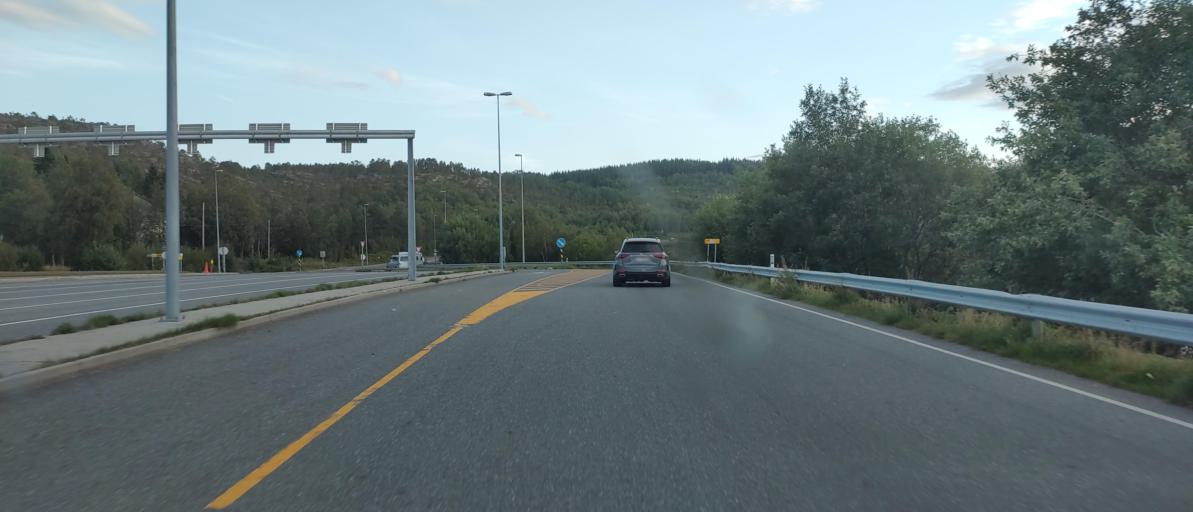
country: NO
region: Nordland
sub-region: Lodingen
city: Lodingen
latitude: 68.2225
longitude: 16.0715
